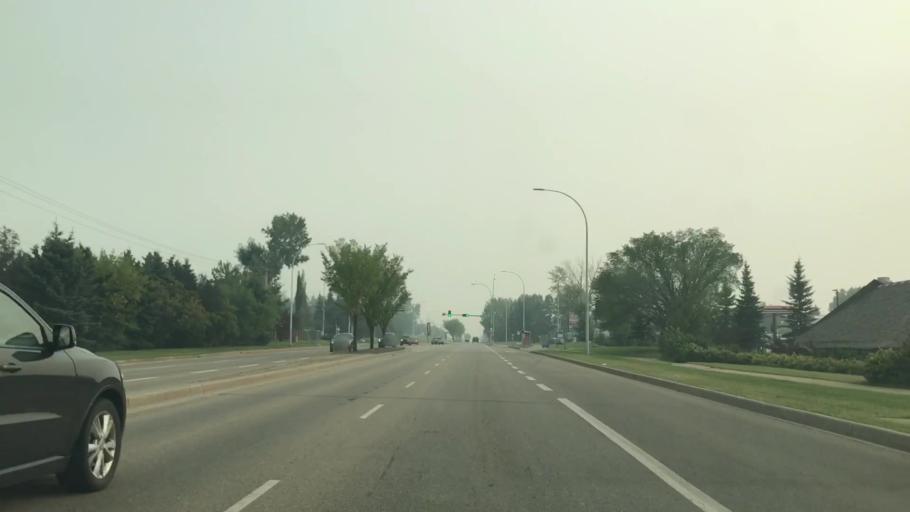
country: CA
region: Alberta
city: Sherwood Park
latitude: 53.5363
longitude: -113.3202
